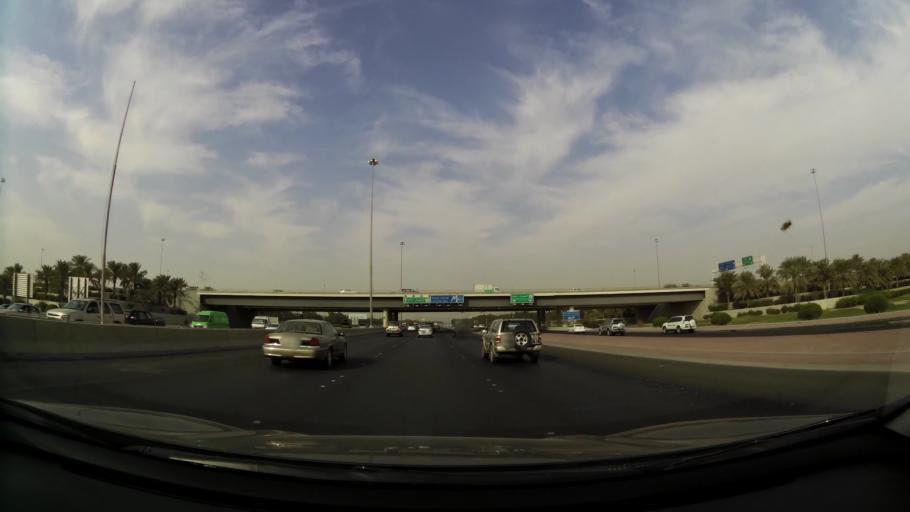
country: KW
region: Al Farwaniyah
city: Janub as Surrah
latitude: 29.2646
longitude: 48.0137
